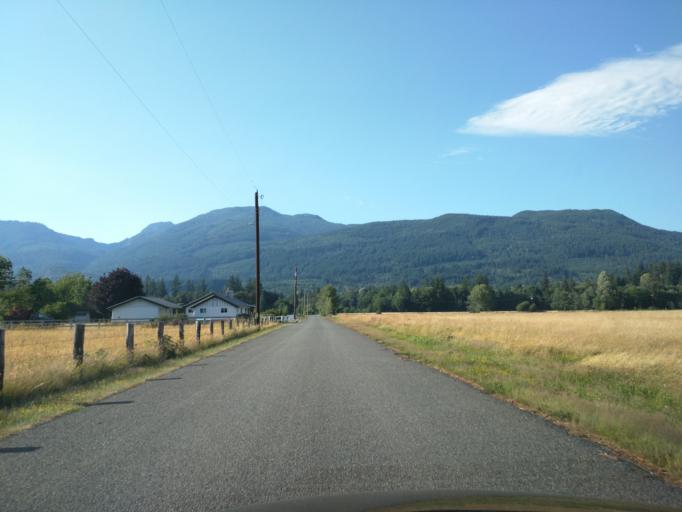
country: US
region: Washington
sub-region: Snohomish County
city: Darrington
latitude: 48.2660
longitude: -121.6815
